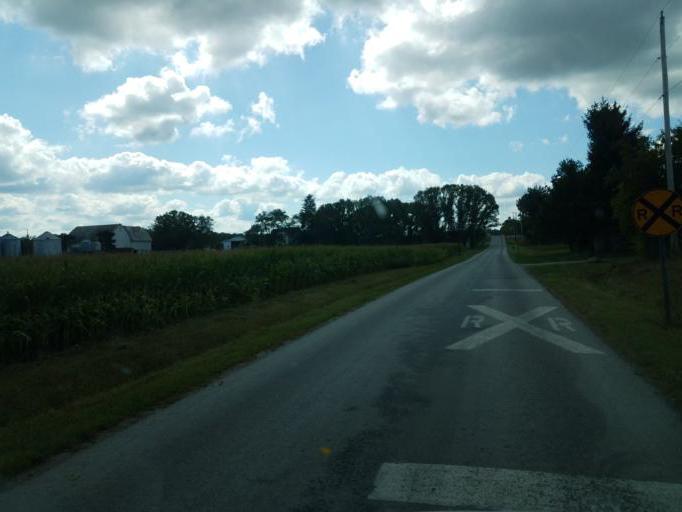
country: US
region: Ohio
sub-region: Medina County
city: Lodi
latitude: 41.0823
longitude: -82.0949
